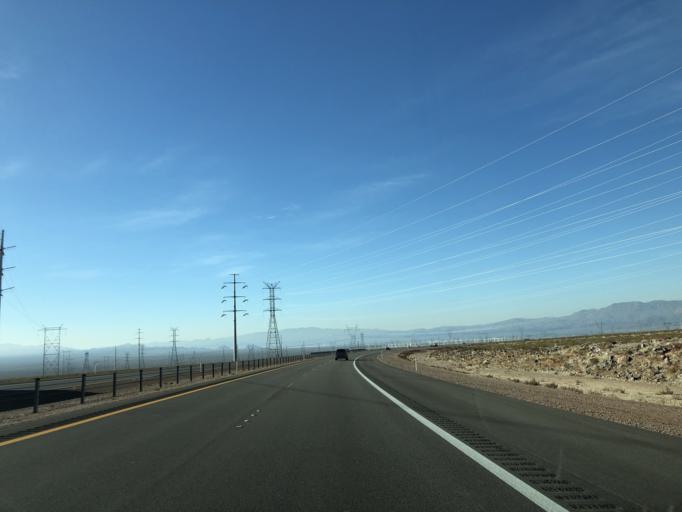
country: US
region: Nevada
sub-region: Clark County
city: Boulder City
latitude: 35.9383
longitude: -114.8130
